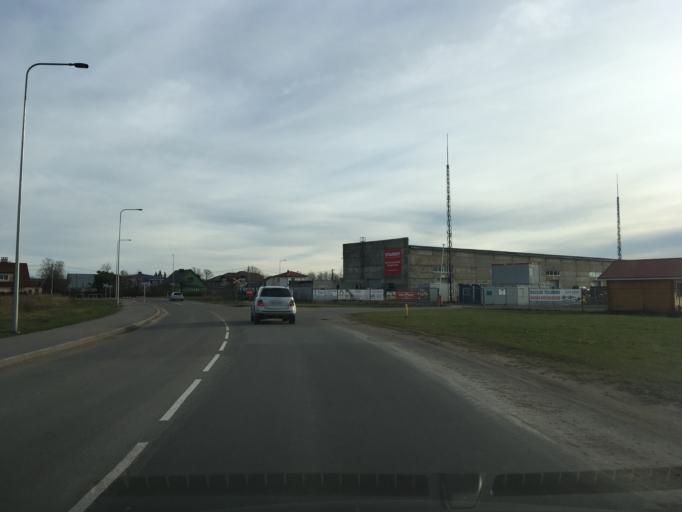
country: EE
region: Ida-Virumaa
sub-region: Narva linn
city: Narva
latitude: 59.3634
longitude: 28.1746
